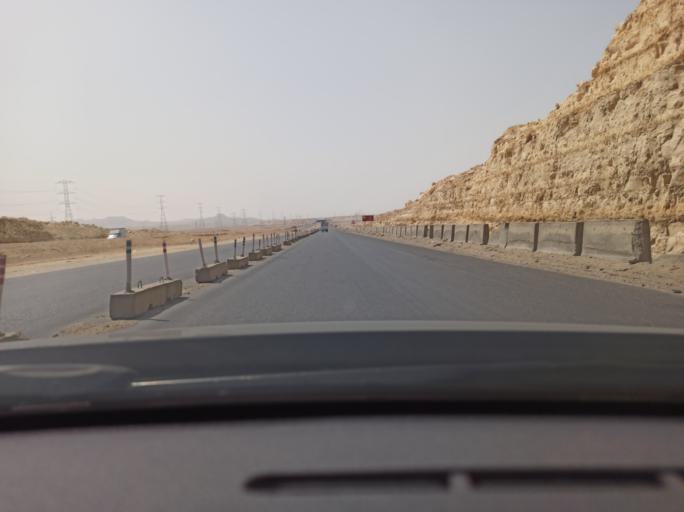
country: EG
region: Muhafazat Bani Suwayf
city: Bush
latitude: 29.1732
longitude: 31.2425
